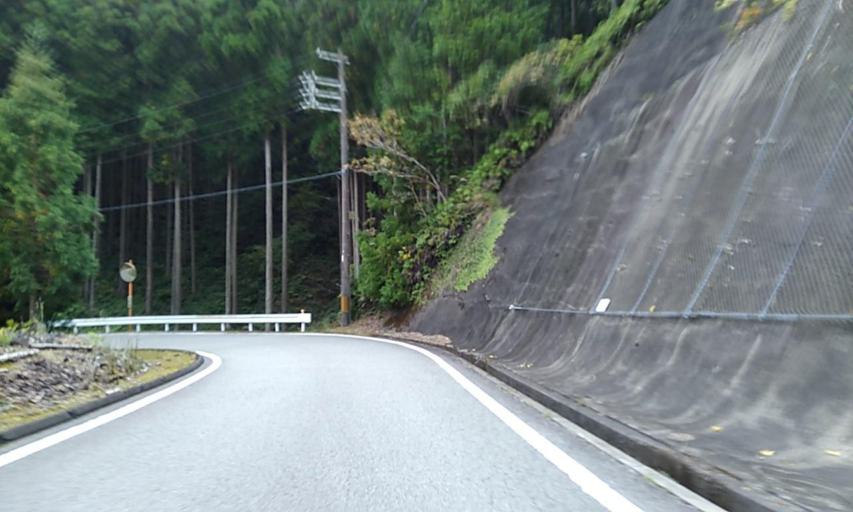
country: JP
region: Wakayama
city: Shingu
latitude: 33.5451
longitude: 135.8474
